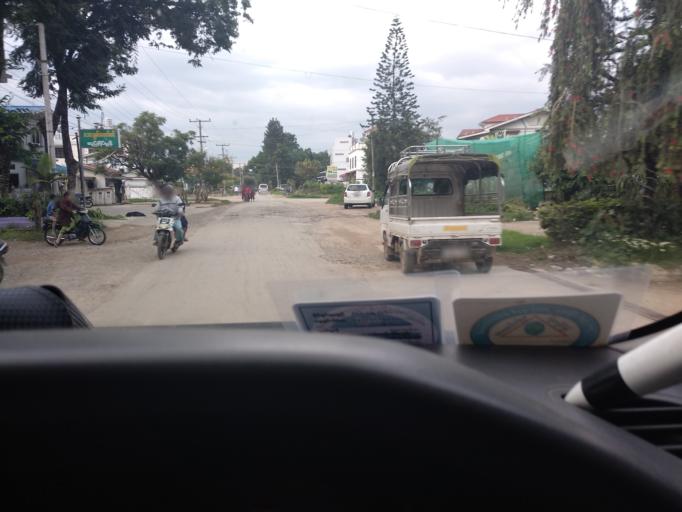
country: MM
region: Mandalay
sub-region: Pyin Oo Lwin District
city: Pyin Oo Lwin
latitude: 22.0332
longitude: 96.4780
